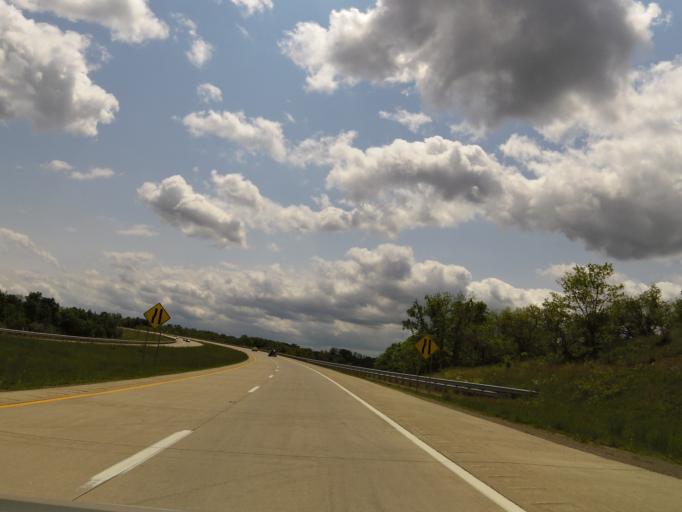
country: US
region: Ohio
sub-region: Athens County
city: Athens
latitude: 39.2782
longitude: -82.0990
